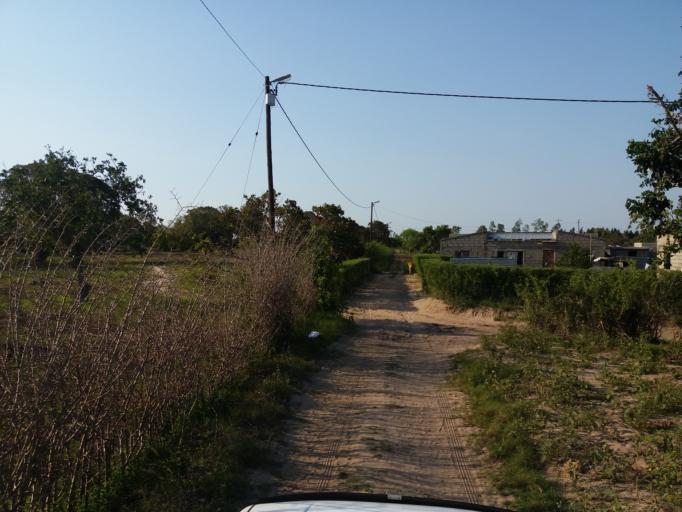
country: MZ
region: Maputo City
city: Maputo
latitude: -25.7613
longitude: 32.6076
